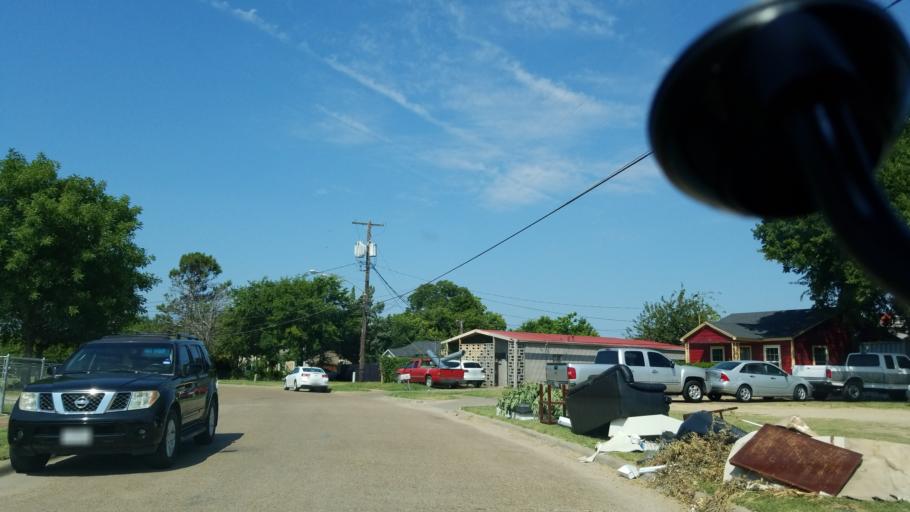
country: US
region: Texas
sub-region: Dallas County
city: Cockrell Hill
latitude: 32.7169
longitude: -96.8774
